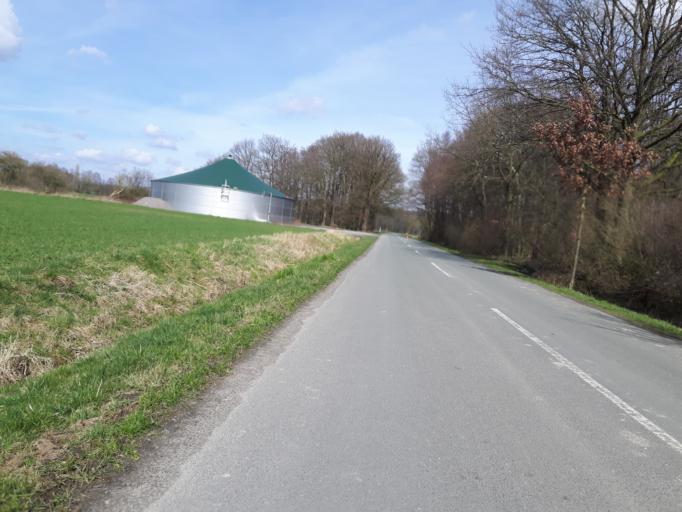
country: DE
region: North Rhine-Westphalia
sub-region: Regierungsbezirk Munster
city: Senden
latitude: 51.8995
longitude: 7.5119
